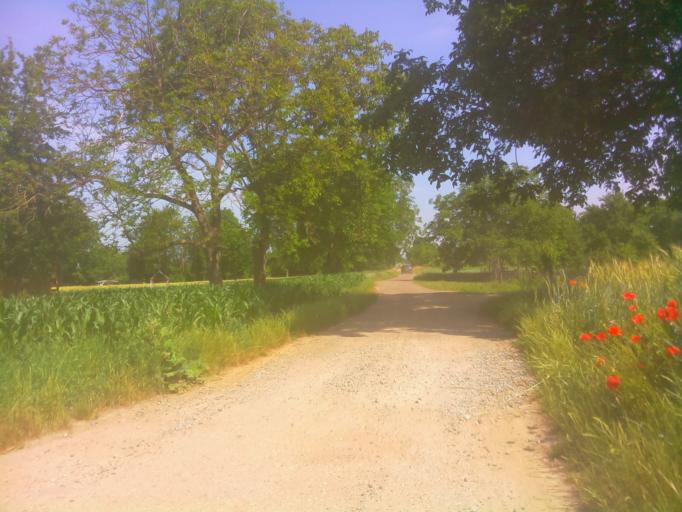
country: DE
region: Baden-Wuerttemberg
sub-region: Karlsruhe Region
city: Weinheim
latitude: 49.5522
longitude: 8.6451
